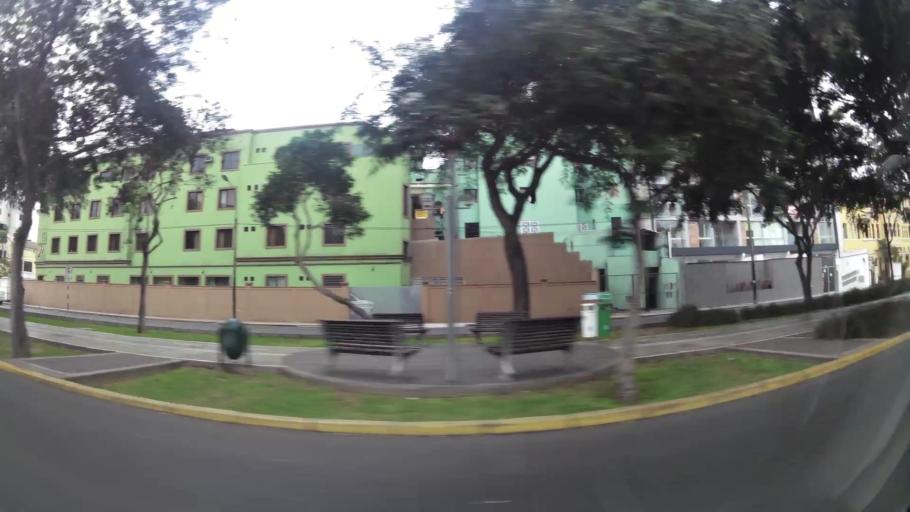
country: PE
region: Lima
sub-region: Lima
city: San Isidro
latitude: -12.1030
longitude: -77.0317
